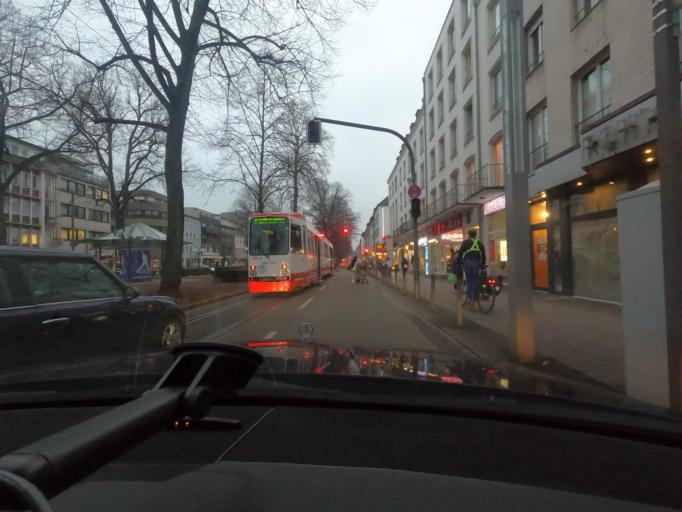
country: DE
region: North Rhine-Westphalia
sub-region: Regierungsbezirk Dusseldorf
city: Krefeld
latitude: 51.3310
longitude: 6.5668
